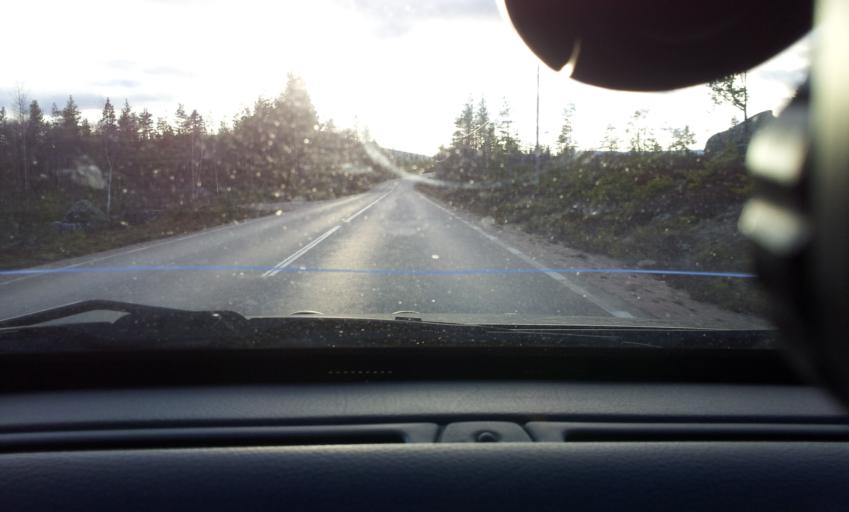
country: SE
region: Jaemtland
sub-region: Harjedalens Kommun
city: Sveg
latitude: 62.1245
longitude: 14.9929
